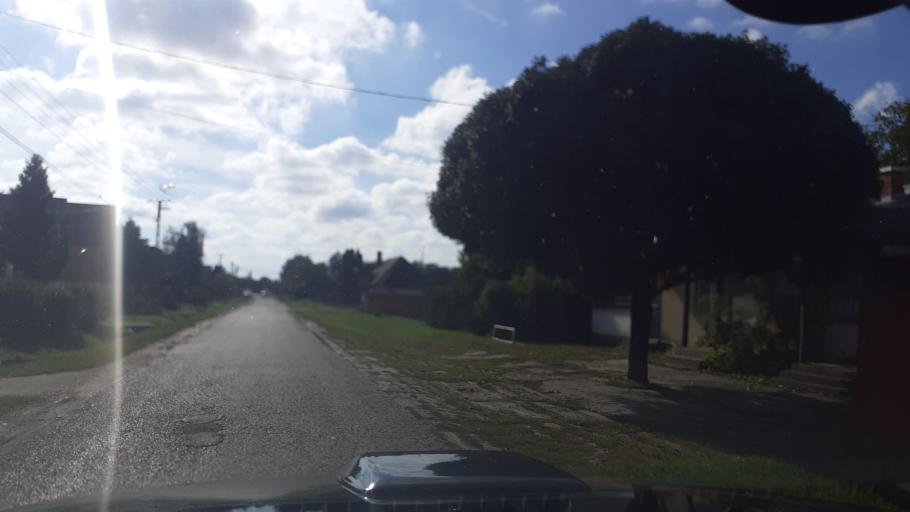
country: HU
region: Fejer
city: Baracs
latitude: 46.9196
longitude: 18.8788
